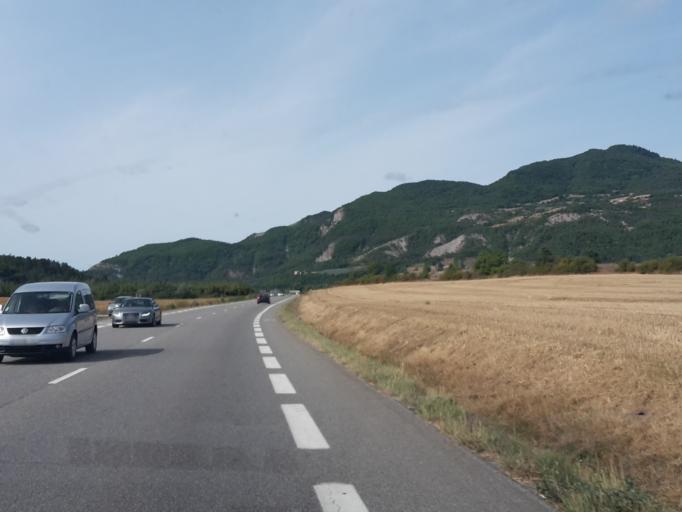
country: FR
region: Provence-Alpes-Cote d'Azur
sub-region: Departement des Hautes-Alpes
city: Tallard
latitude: 44.4527
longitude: 6.0418
